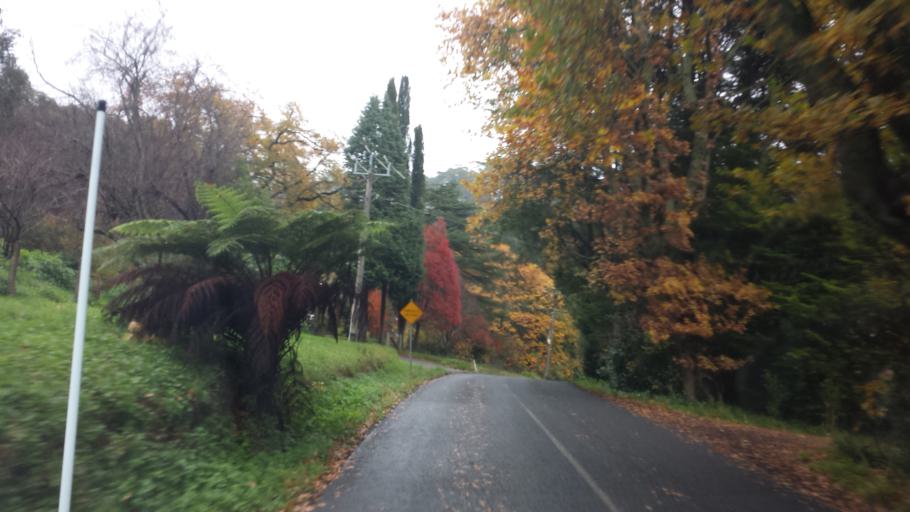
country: AU
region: Victoria
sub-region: Yarra Ranges
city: Monbulk
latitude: -37.8956
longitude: 145.4014
